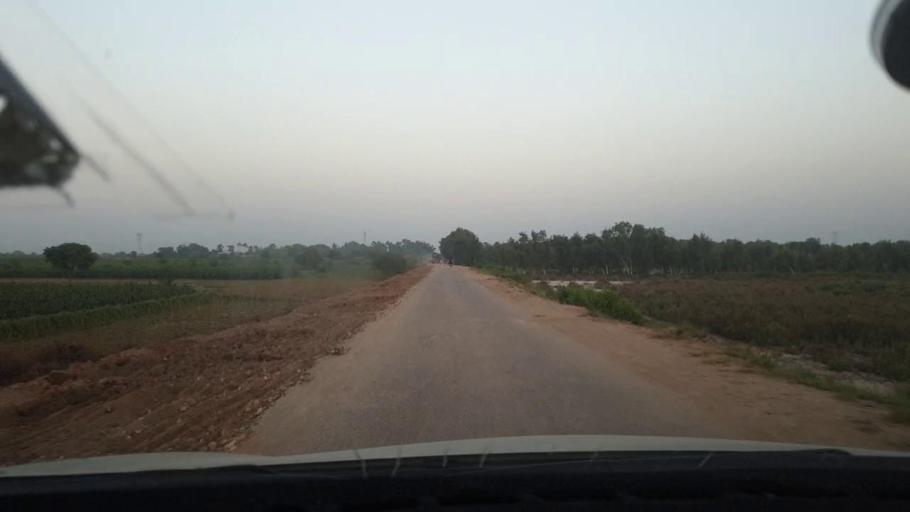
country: PK
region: Sindh
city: Bhit Shah
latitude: 25.7530
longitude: 68.5510
